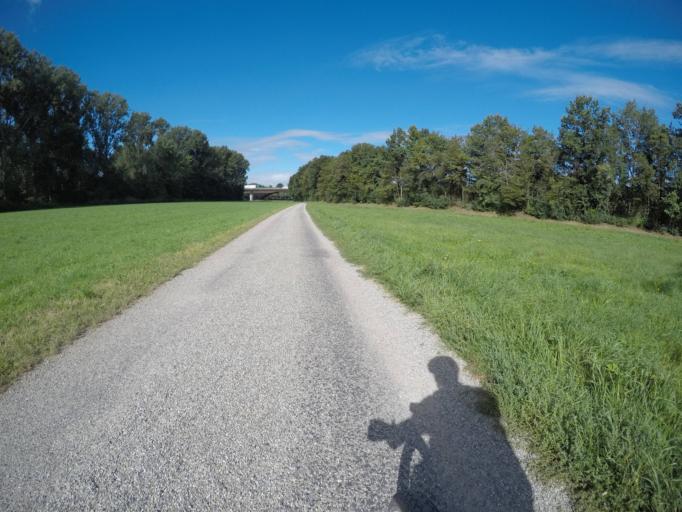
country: DE
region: Baden-Wuerttemberg
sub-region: Regierungsbezirk Stuttgart
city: Freiberg am Neckar
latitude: 48.9422
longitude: 9.2002
